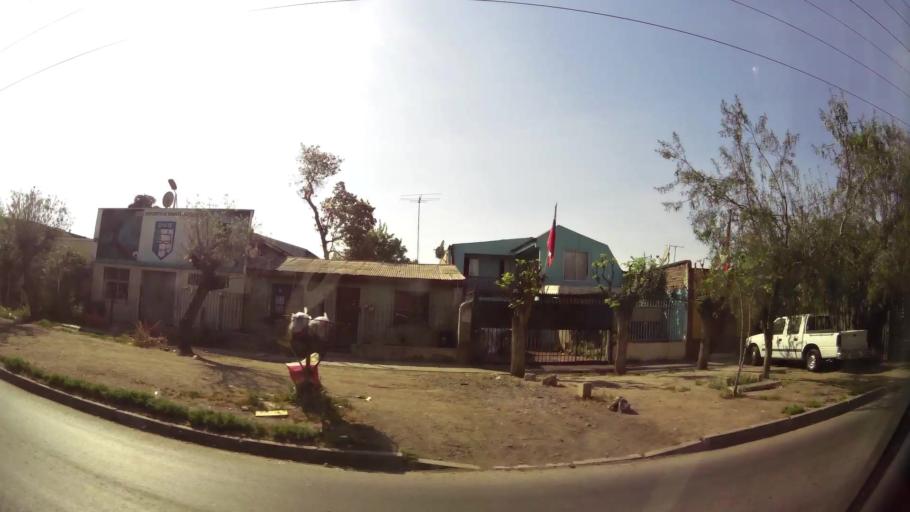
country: CL
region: Santiago Metropolitan
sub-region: Provincia de Santiago
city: Lo Prado
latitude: -33.4263
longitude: -70.7305
